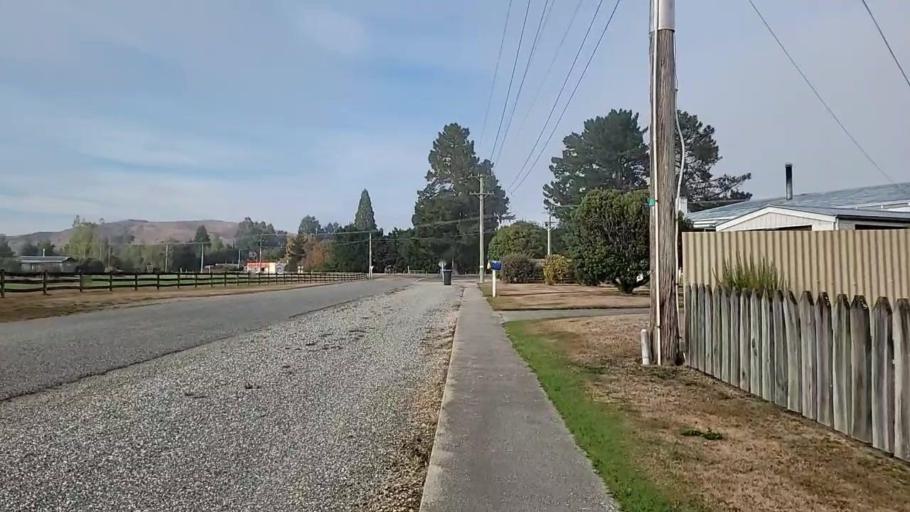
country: NZ
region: Southland
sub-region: Gore District
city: Gore
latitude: -45.6316
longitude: 169.3616
